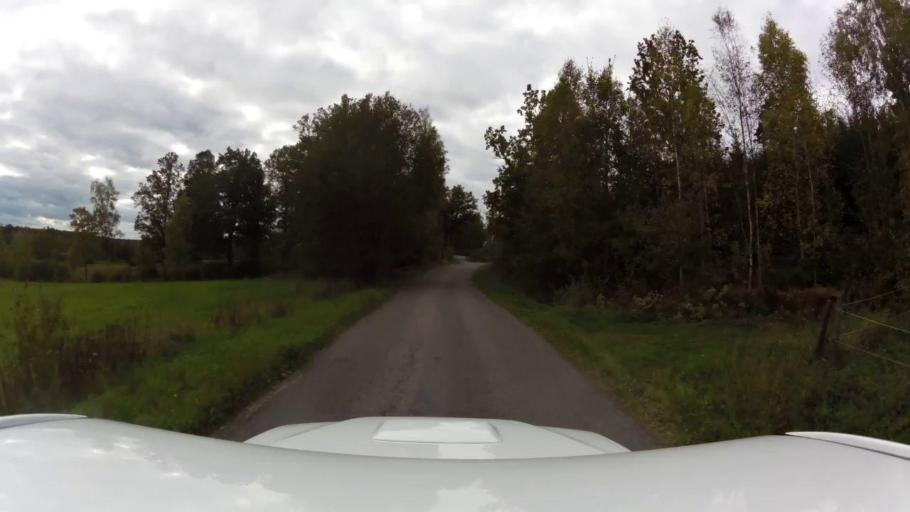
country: SE
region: OEstergoetland
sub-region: Kinda Kommun
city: Rimforsa
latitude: 58.2327
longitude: 15.6281
